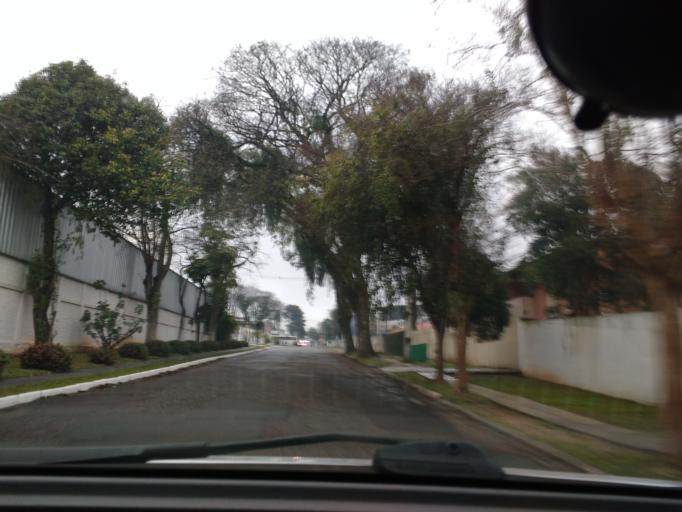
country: BR
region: Parana
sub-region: Pinhais
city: Pinhais
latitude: -25.4269
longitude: -49.2293
